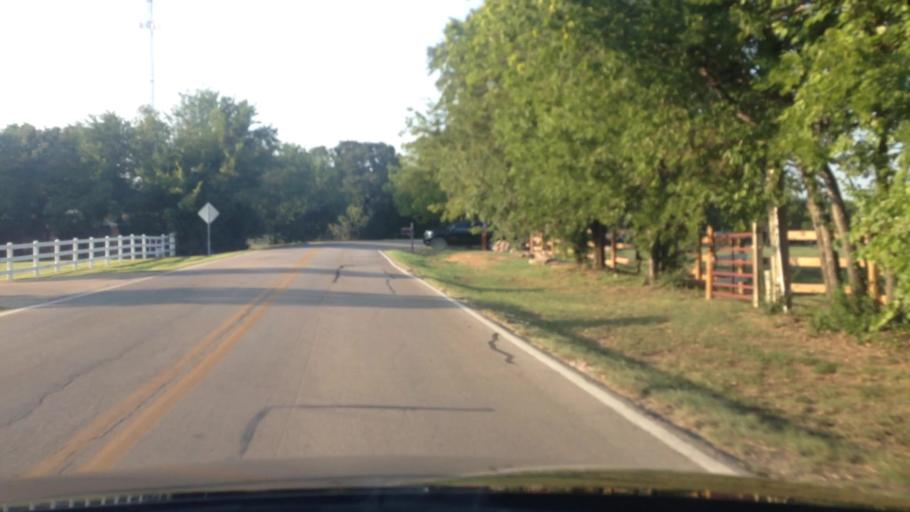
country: US
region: Texas
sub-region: Tarrant County
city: Rendon
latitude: 32.5921
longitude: -97.2595
